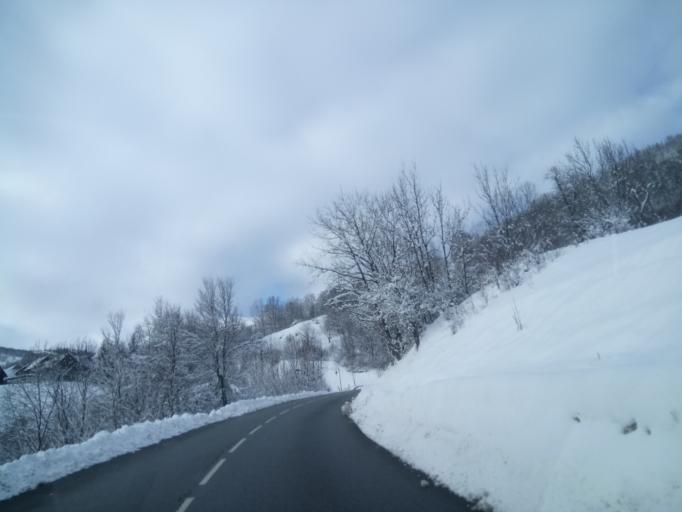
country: FR
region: Rhone-Alpes
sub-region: Departement de la Savoie
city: Saint-Jean-de-Maurienne
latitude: 45.2507
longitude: 6.2974
